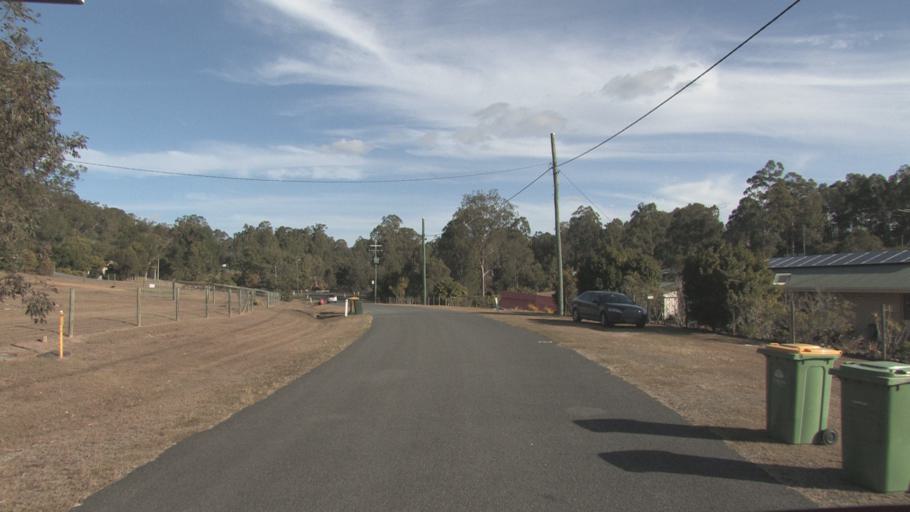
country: AU
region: Queensland
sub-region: Logan
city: Cedar Vale
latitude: -27.8745
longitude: 153.0085
